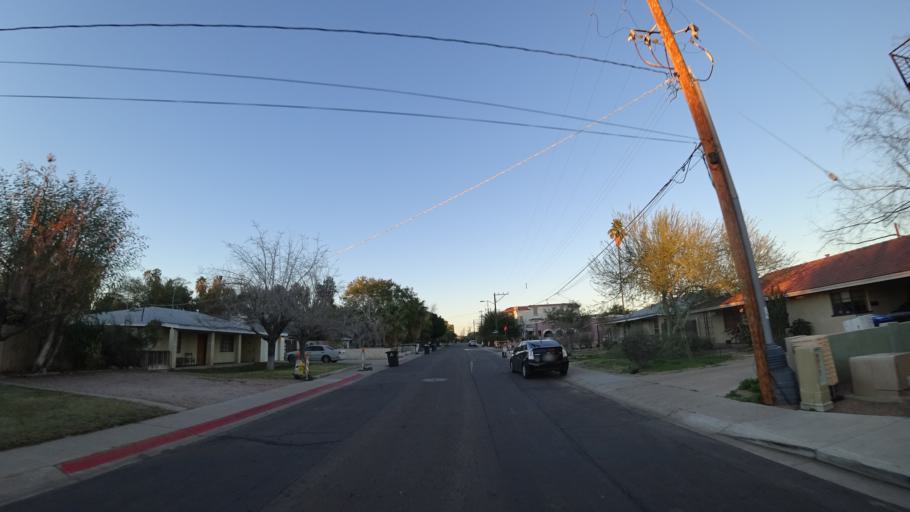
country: US
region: Arizona
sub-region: Maricopa County
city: Tempe Junction
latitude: 33.4258
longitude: -111.9473
